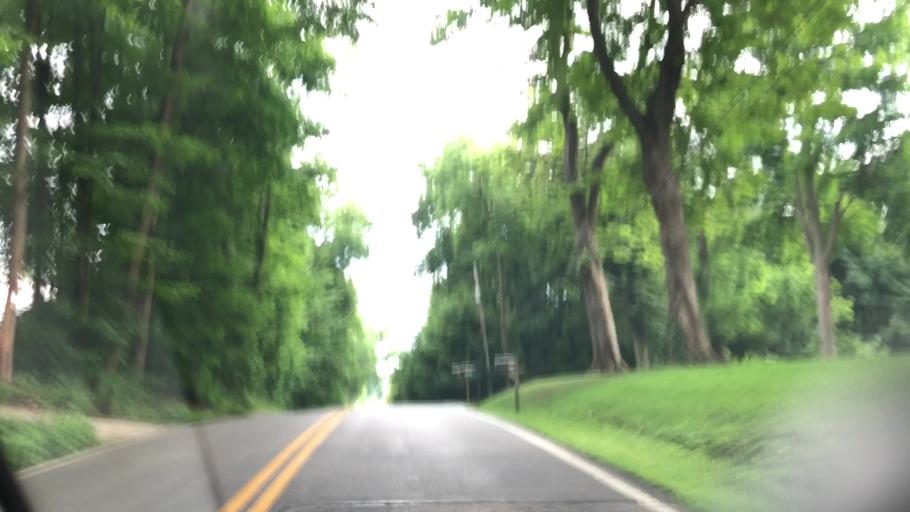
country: US
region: Ohio
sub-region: Summit County
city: Montrose-Ghent
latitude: 41.1242
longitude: -81.7159
